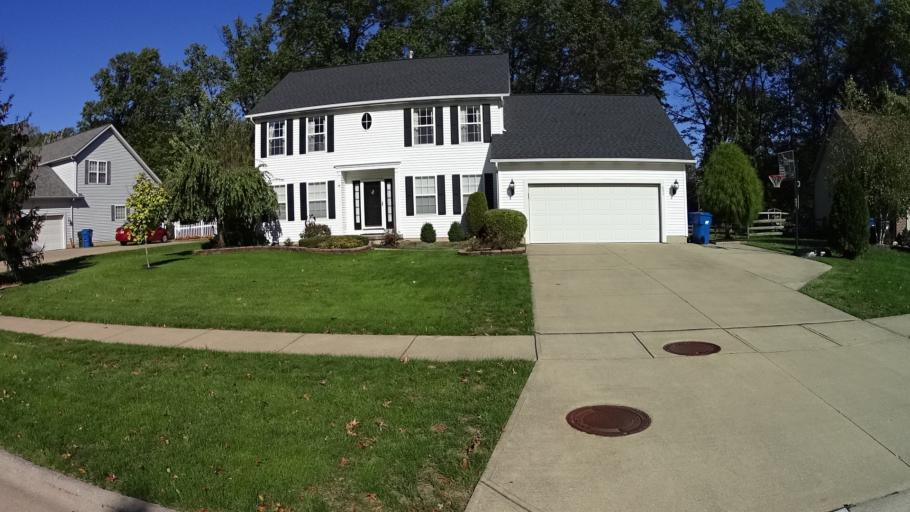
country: US
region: Ohio
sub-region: Lorain County
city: Amherst
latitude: 41.4064
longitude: -82.2494
